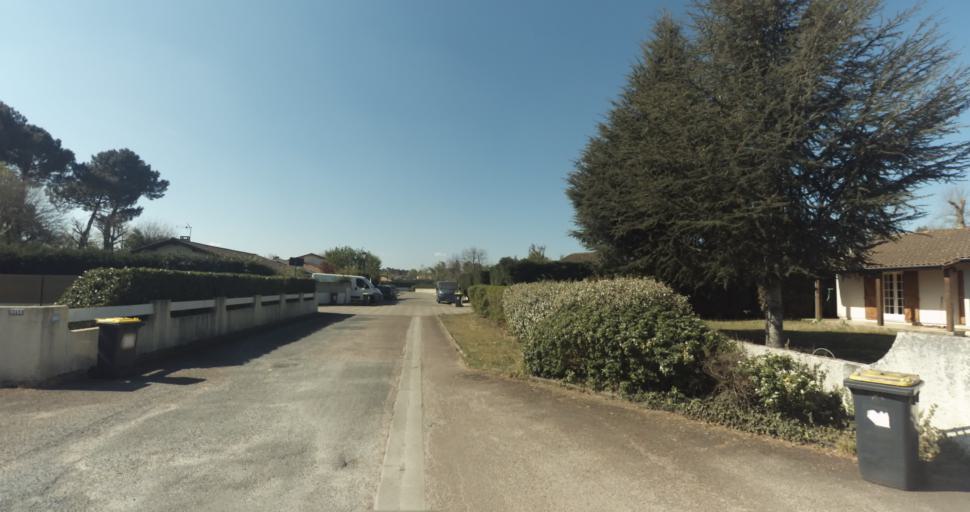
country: FR
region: Aquitaine
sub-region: Departement de la Gironde
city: Martignas-sur-Jalle
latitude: 44.8050
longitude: -0.7807
